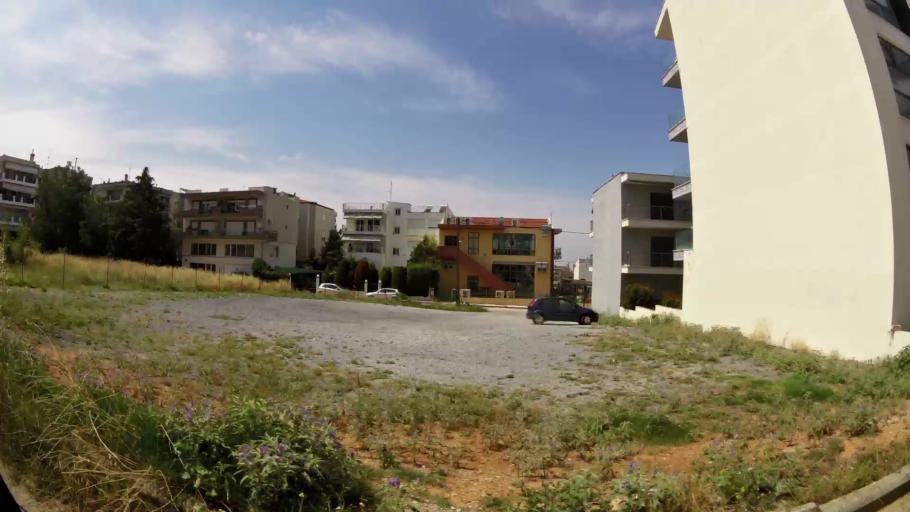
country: GR
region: Central Macedonia
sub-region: Nomos Thessalonikis
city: Pylaia
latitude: 40.6085
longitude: 22.9940
